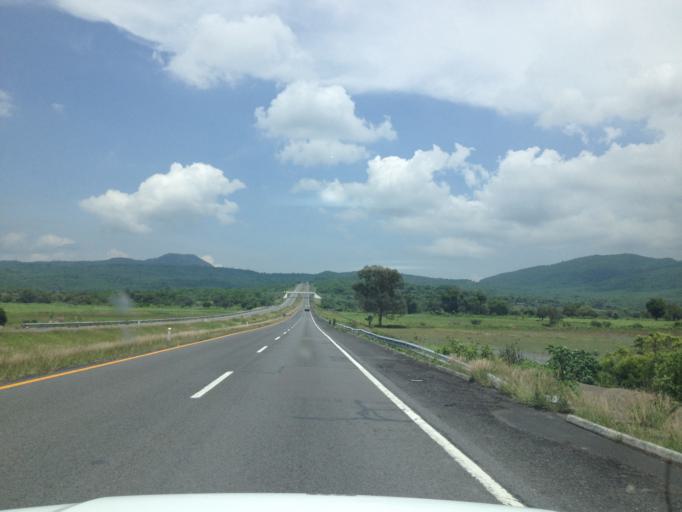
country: MX
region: Mexico
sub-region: Chapultepec
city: Chucandiro
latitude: 19.8748
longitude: -101.3715
